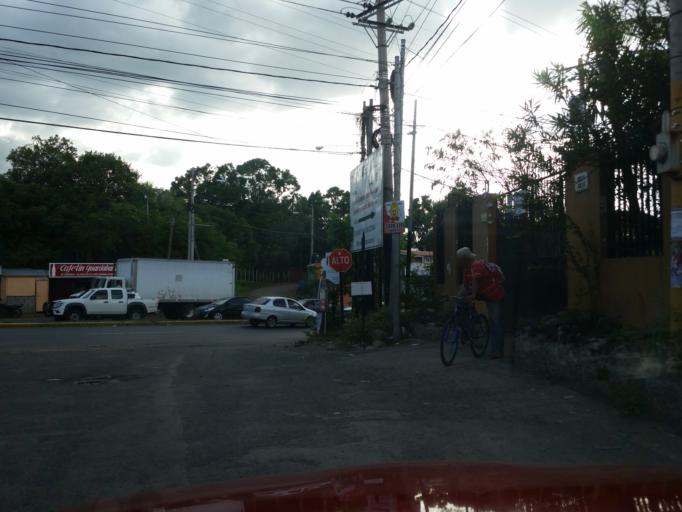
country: NI
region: Masaya
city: Ticuantepe
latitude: 12.0565
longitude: -86.2032
